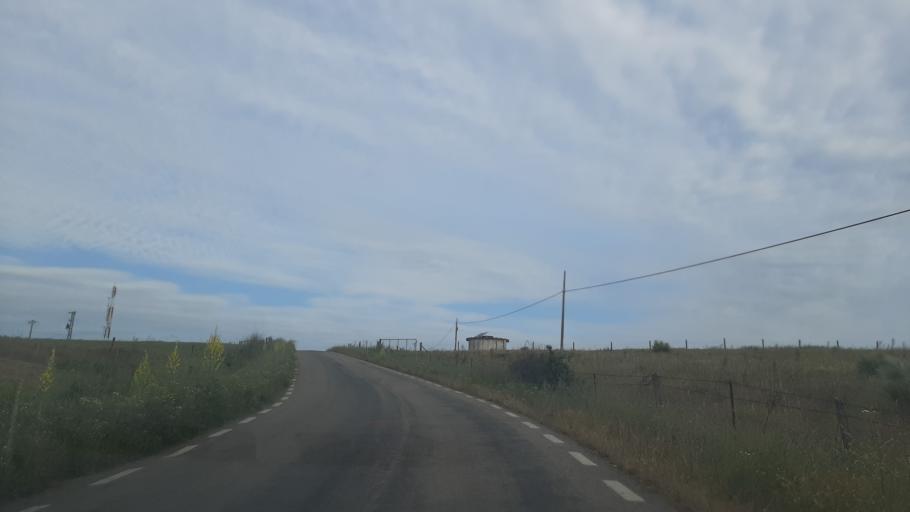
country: ES
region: Castille and Leon
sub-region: Provincia de Salamanca
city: Gallegos de Arganan
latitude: 40.6345
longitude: -6.7120
